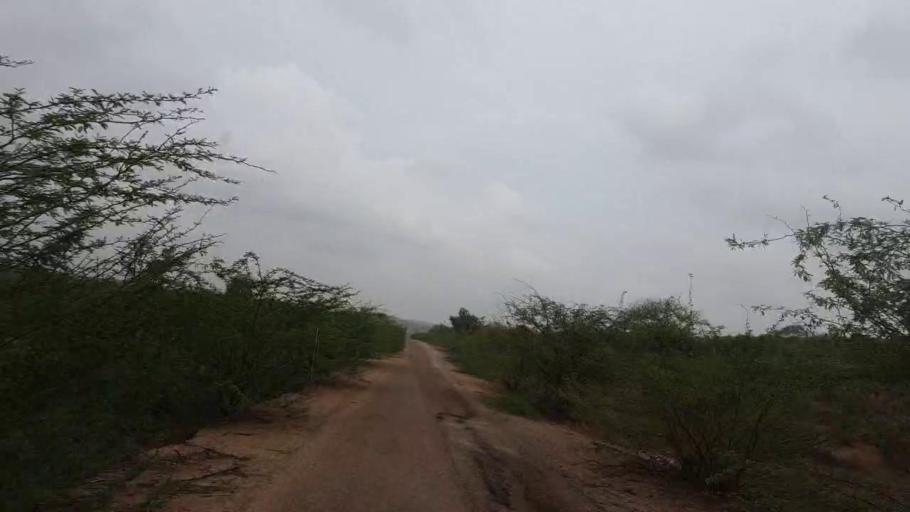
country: PK
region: Sindh
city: Diplo
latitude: 24.5138
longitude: 69.4777
